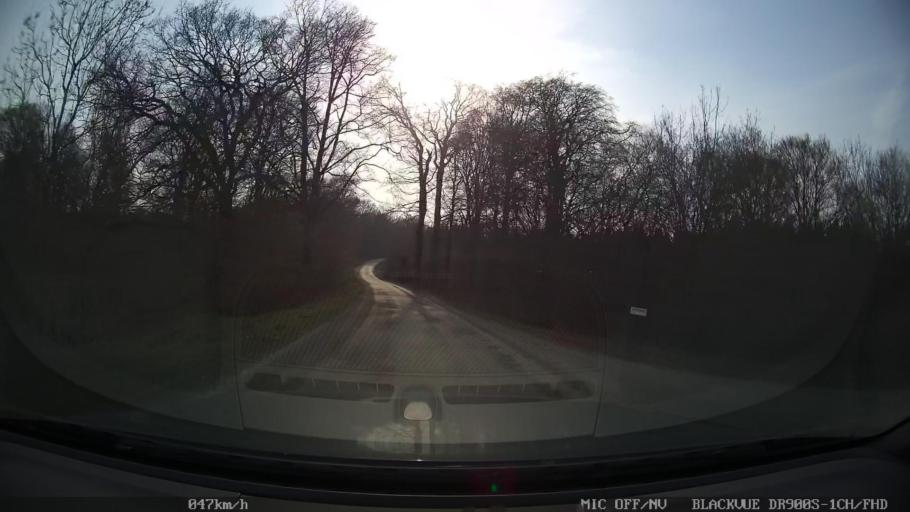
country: SE
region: Skane
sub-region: Ystads Kommun
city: Ystad
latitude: 55.4591
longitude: 13.7831
